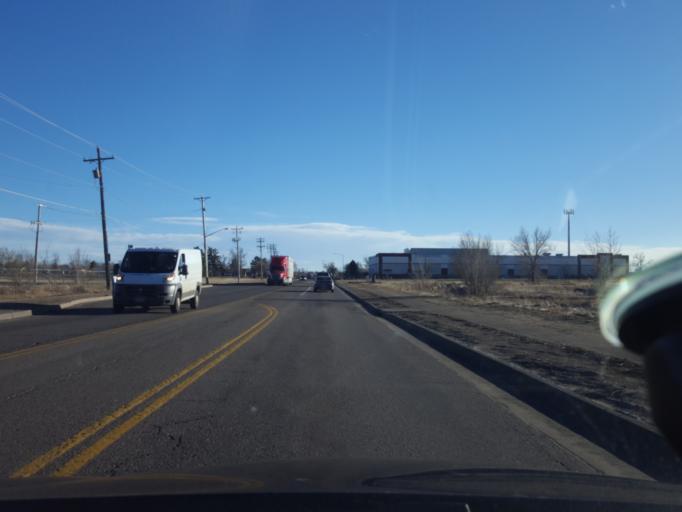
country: US
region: Colorado
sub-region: Adams County
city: Aurora
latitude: 39.7514
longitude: -104.7724
